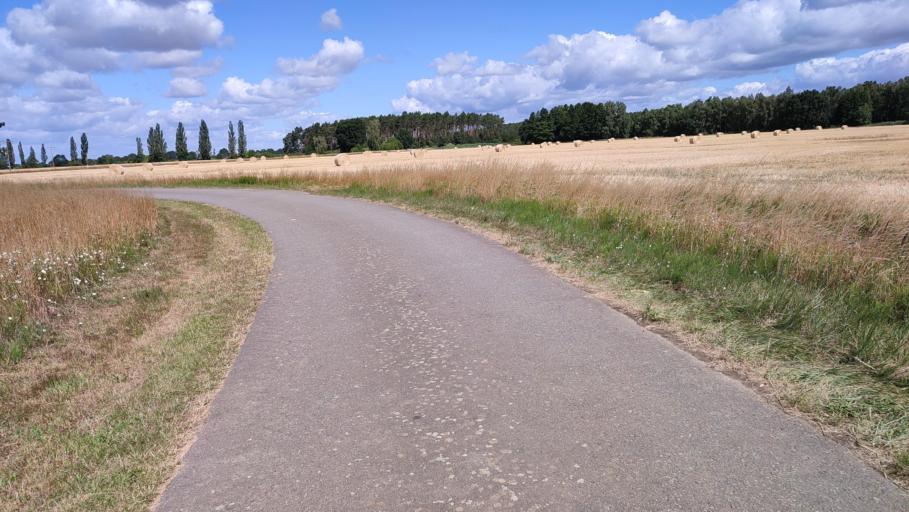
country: DE
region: Lower Saxony
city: Neu Darchau
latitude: 53.2298
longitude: 10.9736
